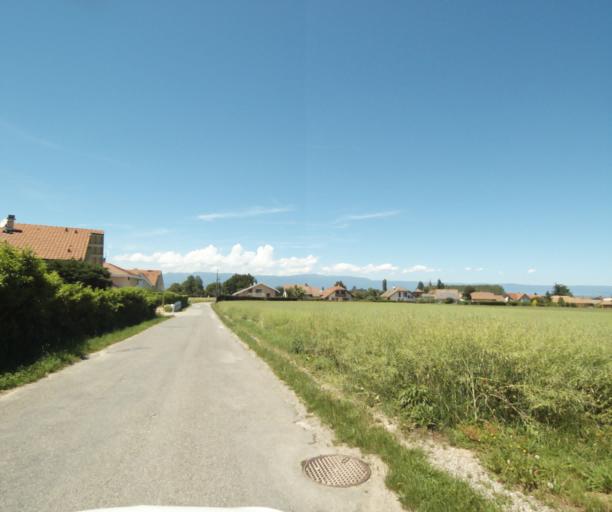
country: FR
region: Rhone-Alpes
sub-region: Departement de la Haute-Savoie
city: Veigy-Foncenex
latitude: 46.2615
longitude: 6.2586
